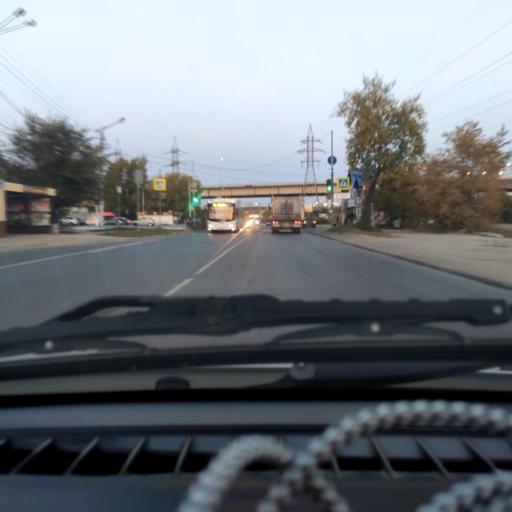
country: RU
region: Samara
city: Zhigulevsk
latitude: 53.4794
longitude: 49.5160
